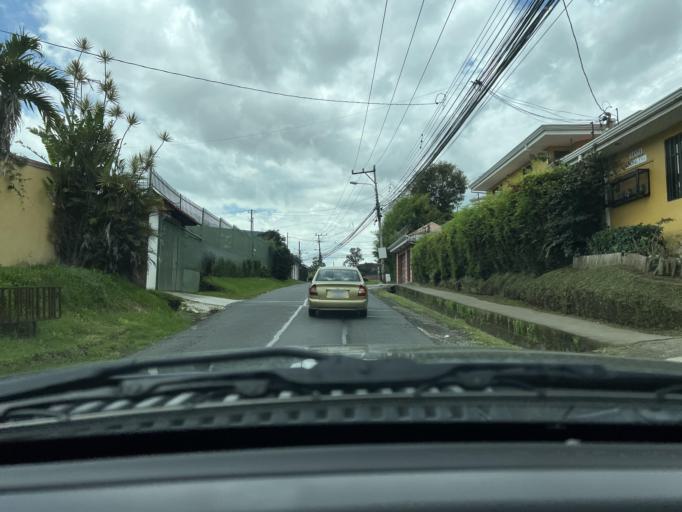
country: CR
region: San Jose
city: Granadilla
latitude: 9.9394
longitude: -84.0253
